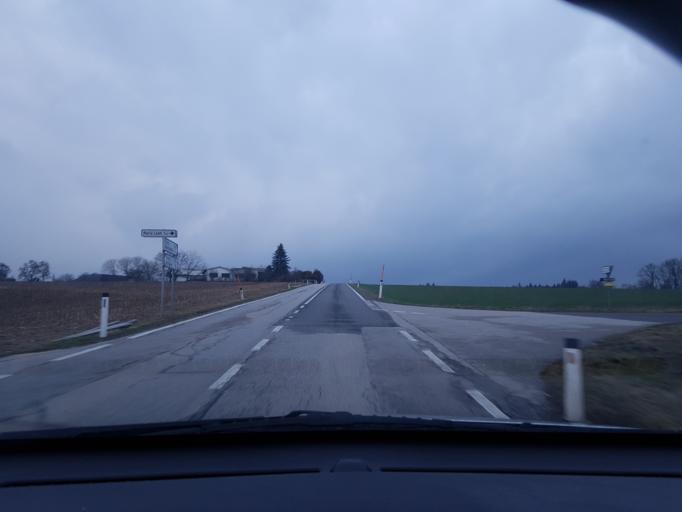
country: AT
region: Upper Austria
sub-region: Politischer Bezirk Steyr-Land
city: Sierning
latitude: 48.1195
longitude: 14.3477
